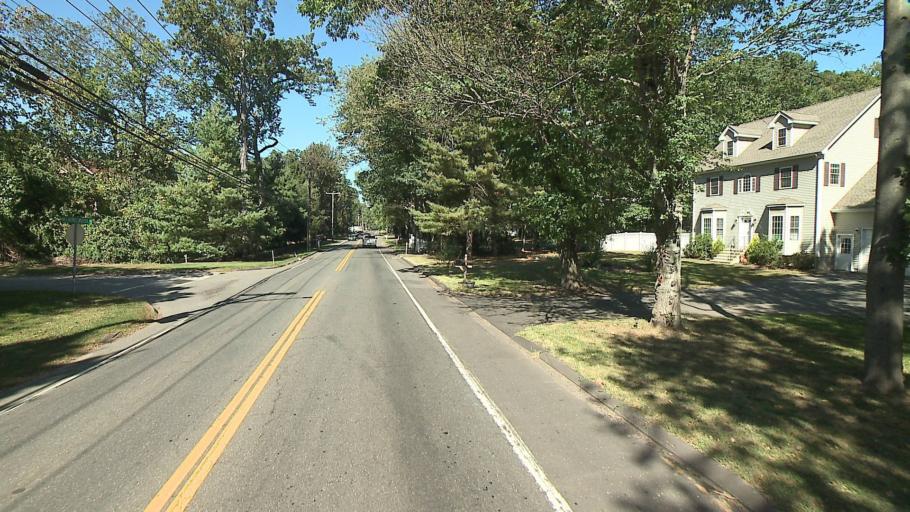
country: US
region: Connecticut
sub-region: New Haven County
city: Orange
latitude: 41.3012
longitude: -73.0433
